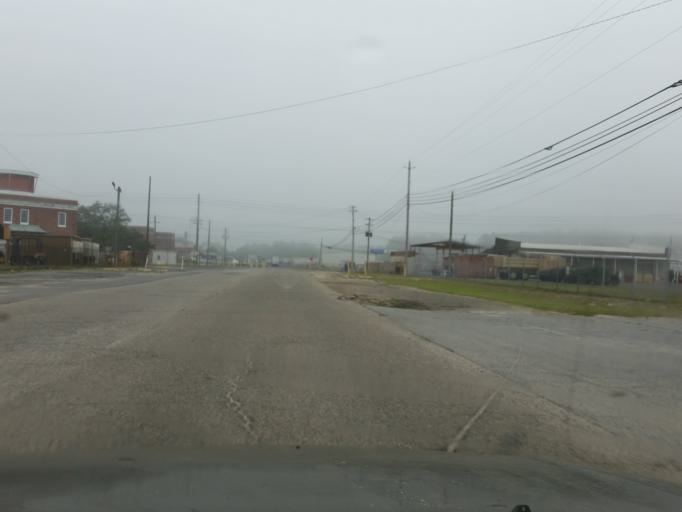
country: US
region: Florida
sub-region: Escambia County
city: Ferry Pass
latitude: 30.5260
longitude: -87.1977
